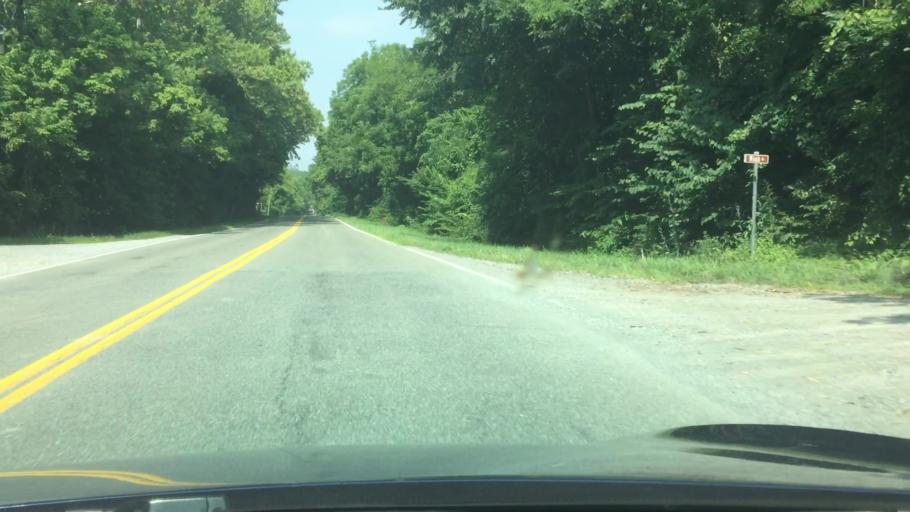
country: US
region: Virginia
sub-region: Pulaski County
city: Pulaski
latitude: 36.9500
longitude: -80.9070
